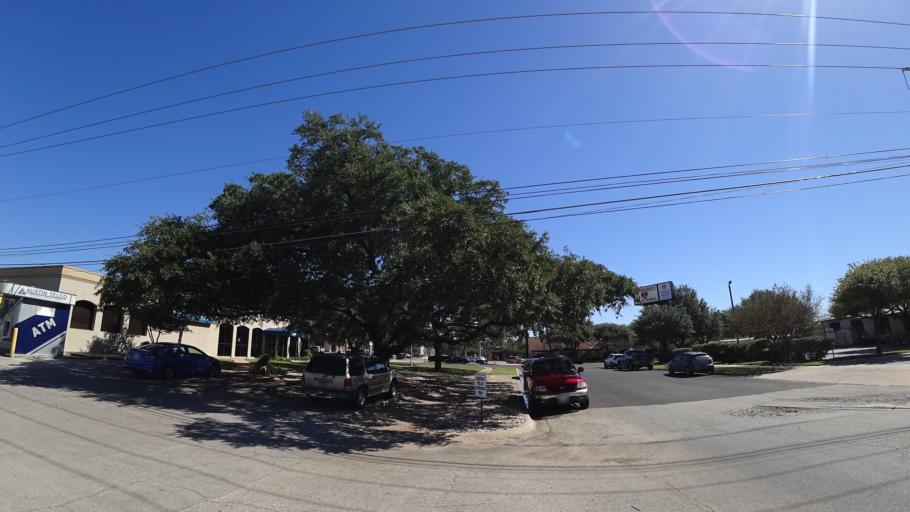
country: US
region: Texas
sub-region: Travis County
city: Rollingwood
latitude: 30.2320
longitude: -97.7957
